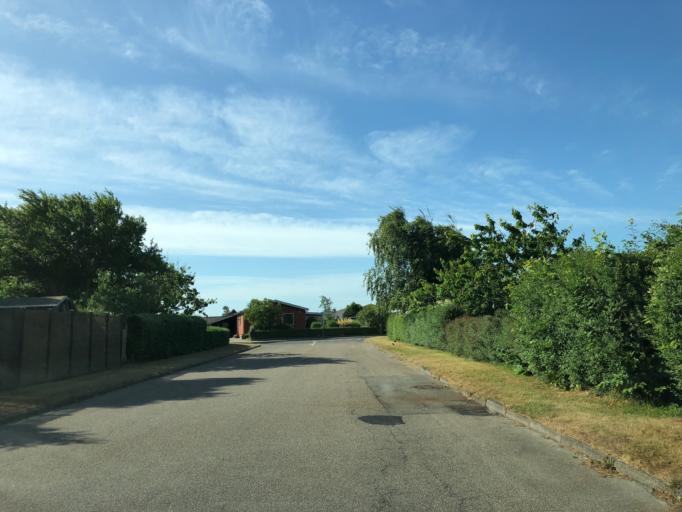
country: DK
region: Central Jutland
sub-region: Holstebro Kommune
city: Ulfborg
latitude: 56.3406
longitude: 8.3396
